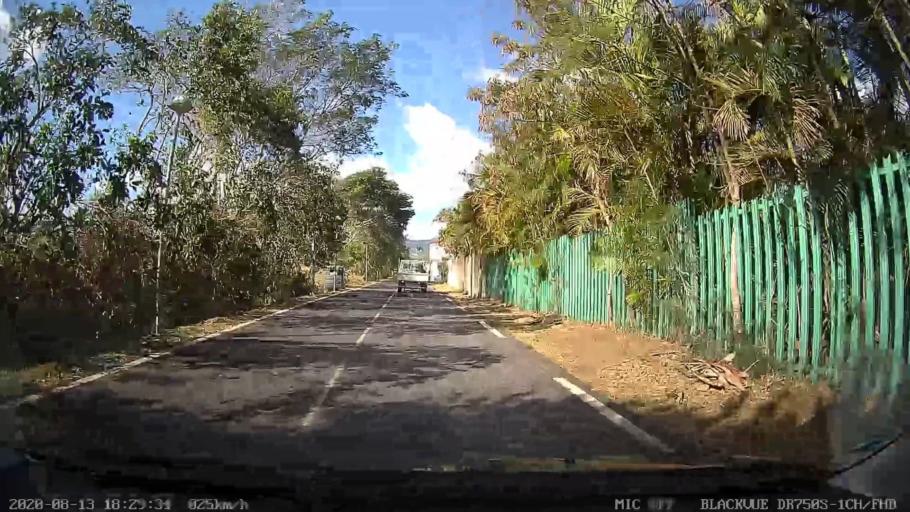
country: RE
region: Reunion
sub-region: Reunion
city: Sainte-Marie
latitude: -20.8969
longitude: 55.5371
